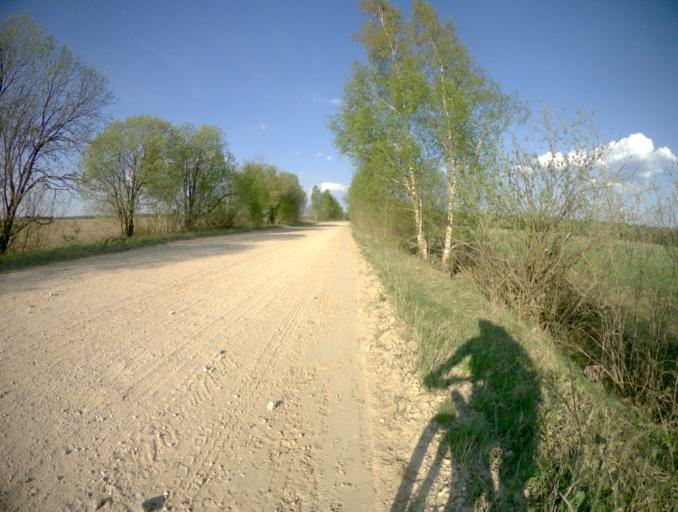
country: RU
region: Vladimir
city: Mstera
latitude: 56.5445
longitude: 41.6551
